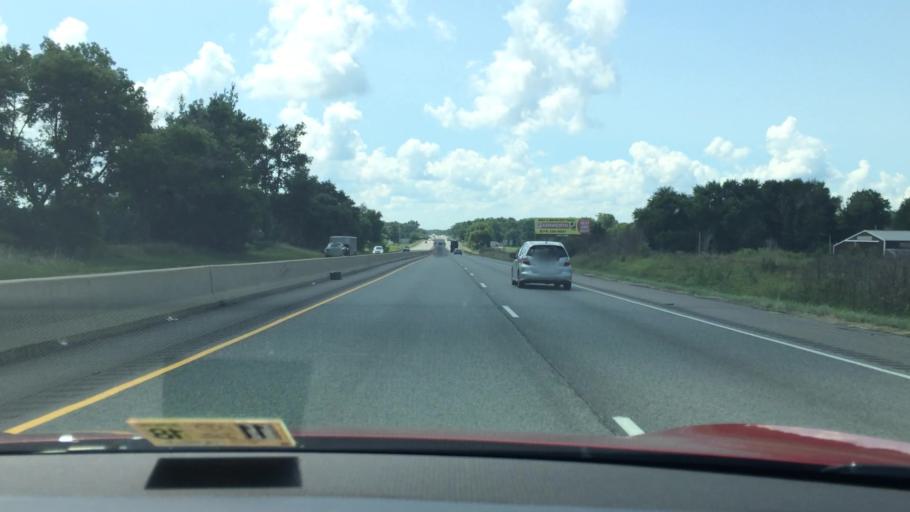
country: US
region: Indiana
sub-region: Saint Joseph County
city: South Bend
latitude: 41.6998
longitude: -86.3403
